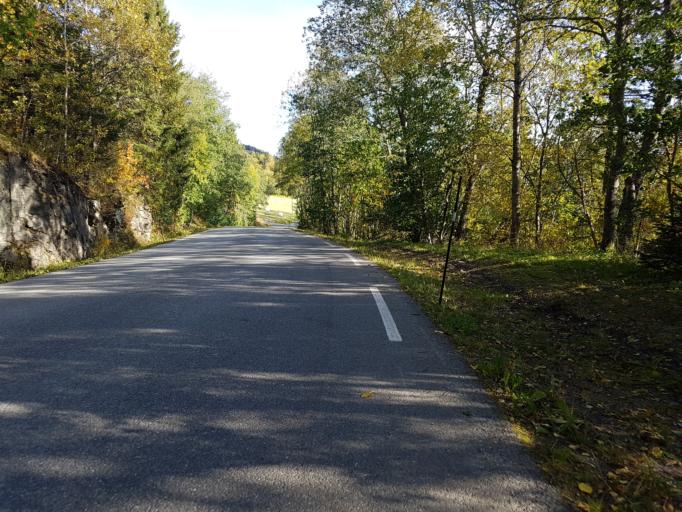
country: NO
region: Sor-Trondelag
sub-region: Malvik
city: Malvik
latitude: 63.3839
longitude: 10.5872
